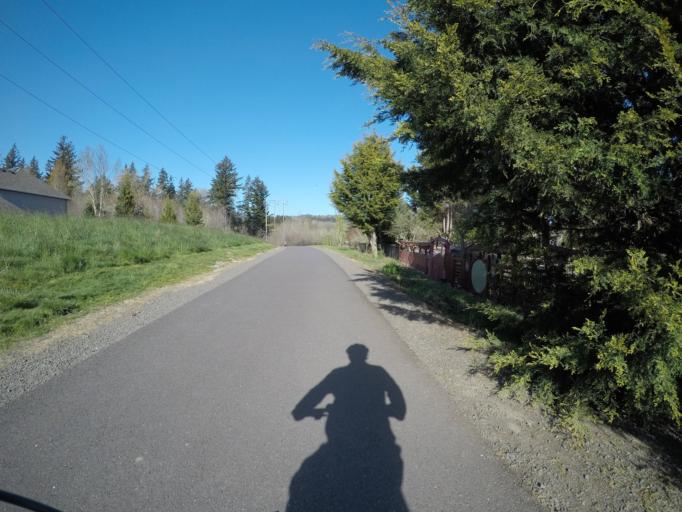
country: US
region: Oregon
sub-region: Washington County
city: Oak Hills
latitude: 45.5613
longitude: -122.8279
